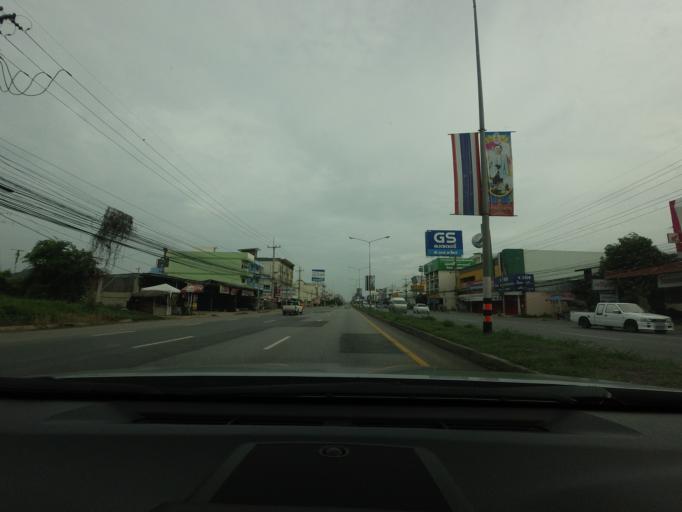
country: TH
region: Phetchaburi
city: Tha Yang
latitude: 12.9684
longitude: 99.8996
